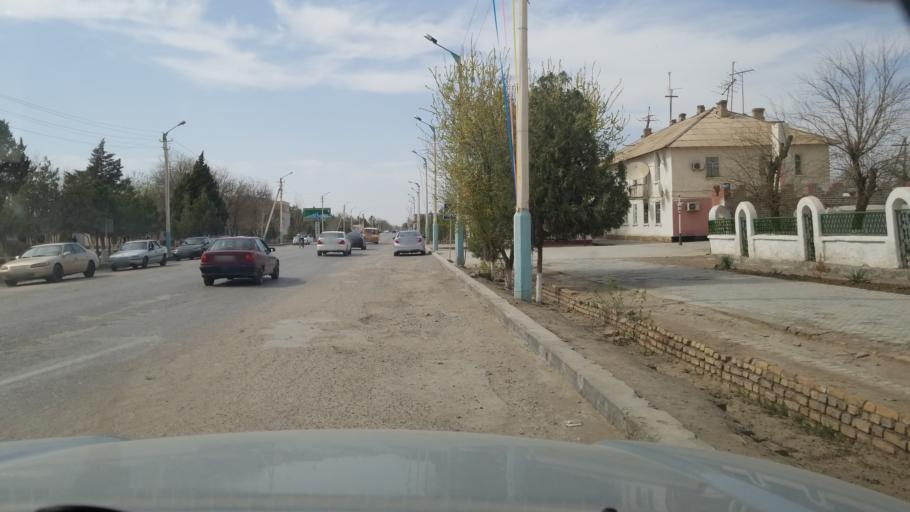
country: TM
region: Lebap
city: Atamyrat
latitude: 37.8392
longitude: 65.2097
